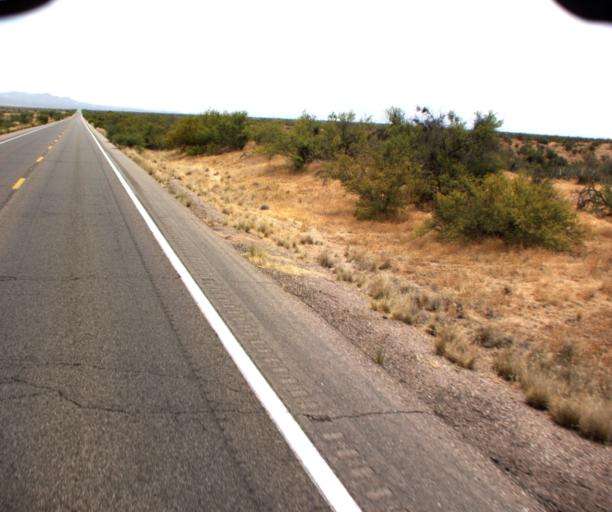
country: US
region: Arizona
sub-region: Gila County
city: Peridot
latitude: 33.3207
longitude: -110.5373
